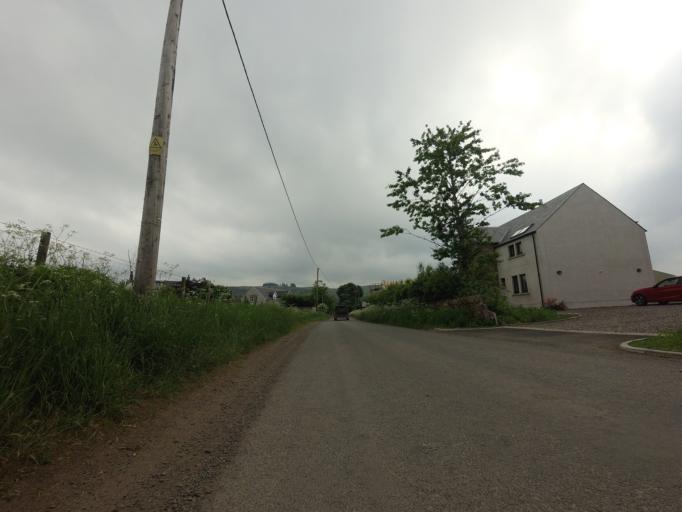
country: GB
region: Scotland
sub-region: Perth and Kinross
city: Kinross
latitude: 56.1701
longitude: -3.4461
